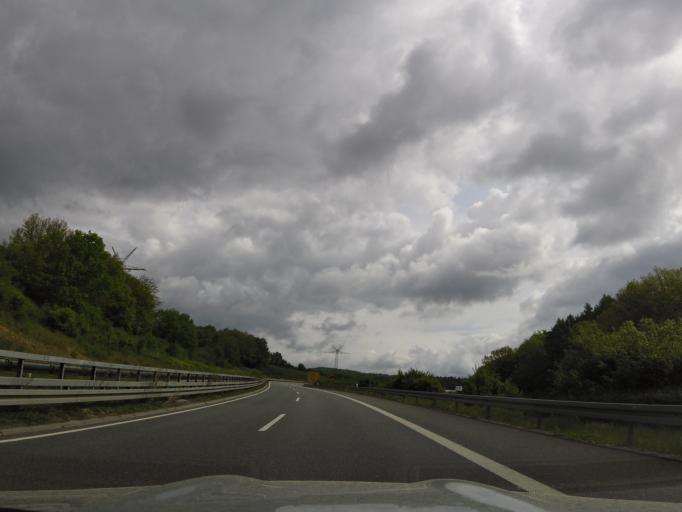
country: DE
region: Hesse
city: Merenberg
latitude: 50.4960
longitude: 8.1836
